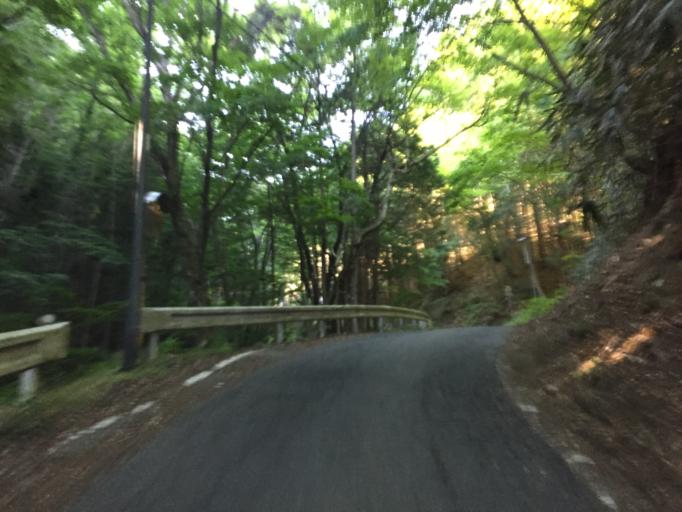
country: JP
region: Ibaraki
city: Kitaibaraki
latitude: 36.8935
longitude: 140.6212
